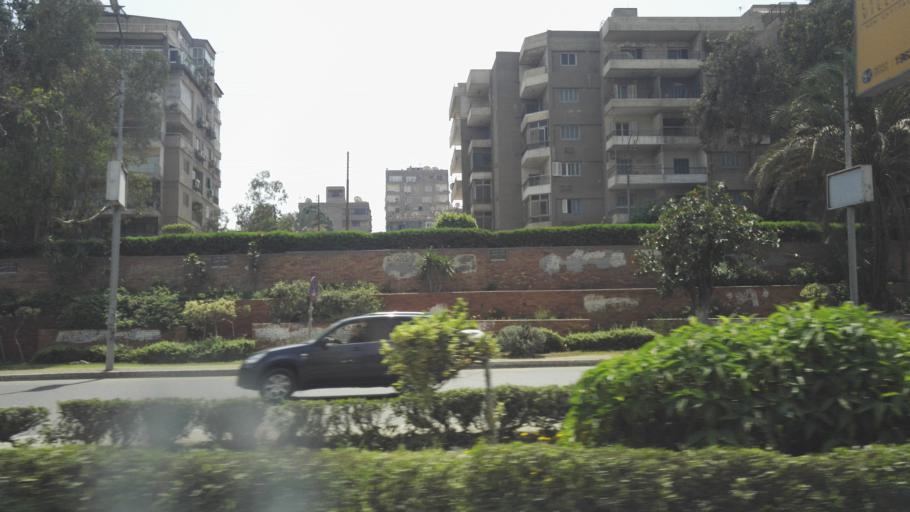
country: EG
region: Muhafazat al Qahirah
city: Cairo
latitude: 30.0842
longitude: 31.3397
